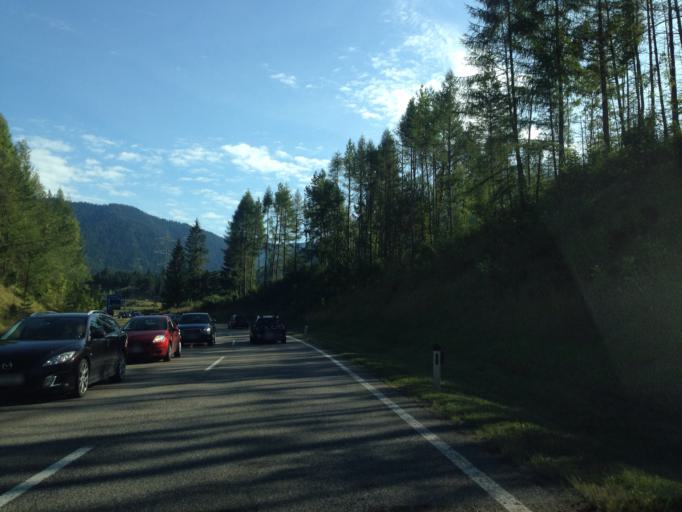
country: AT
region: Tyrol
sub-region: Politischer Bezirk Reutte
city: Breitenwang
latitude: 47.4857
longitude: 10.7415
